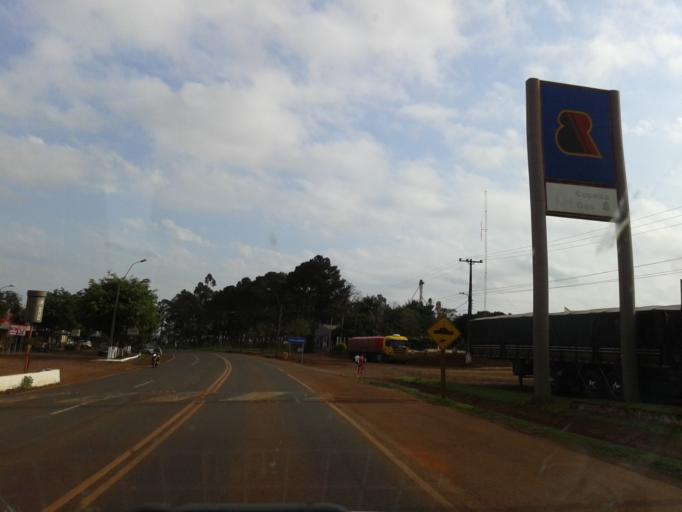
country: PY
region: Itapua
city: Edelira
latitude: -26.7236
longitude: -55.3460
